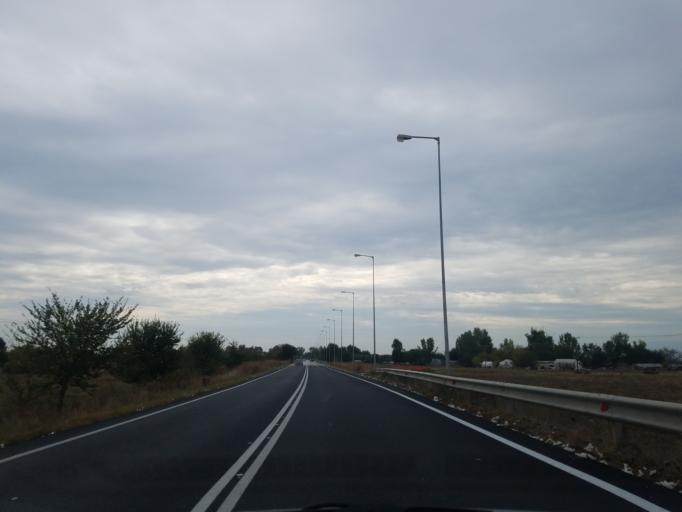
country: GR
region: Thessaly
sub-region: Nomos Kardhitsas
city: Agnantero
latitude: 39.4829
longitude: 21.8387
